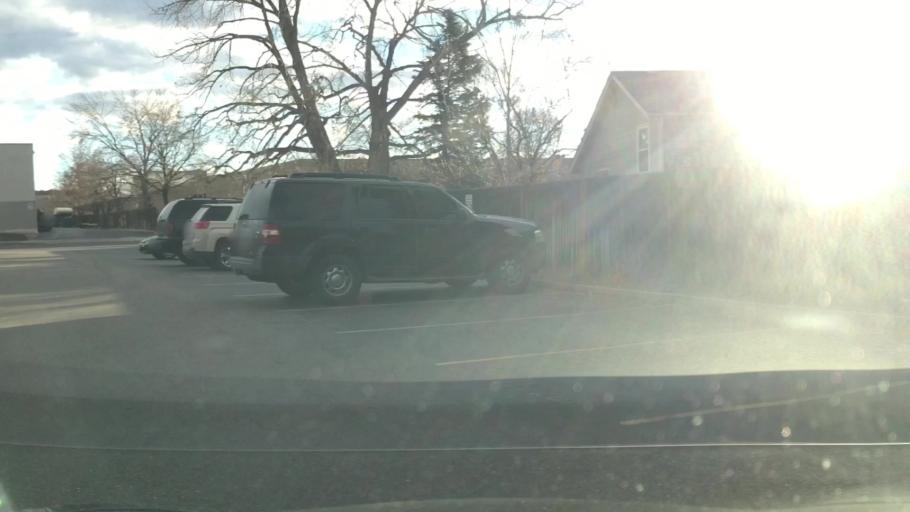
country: US
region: Colorado
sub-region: Adams County
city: Aurora
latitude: 39.6622
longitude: -104.8482
